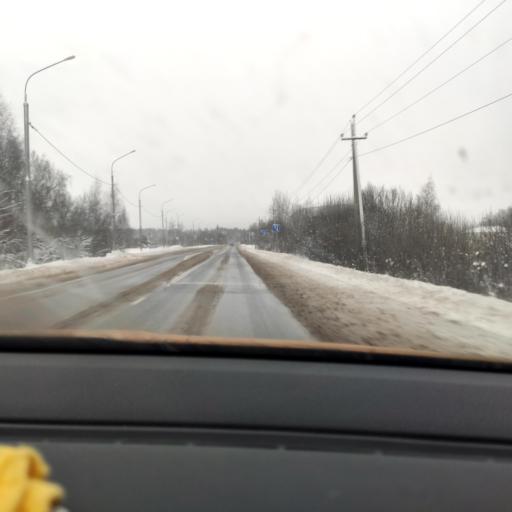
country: RU
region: Moskovskaya
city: Yershovo
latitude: 55.7572
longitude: 36.8688
